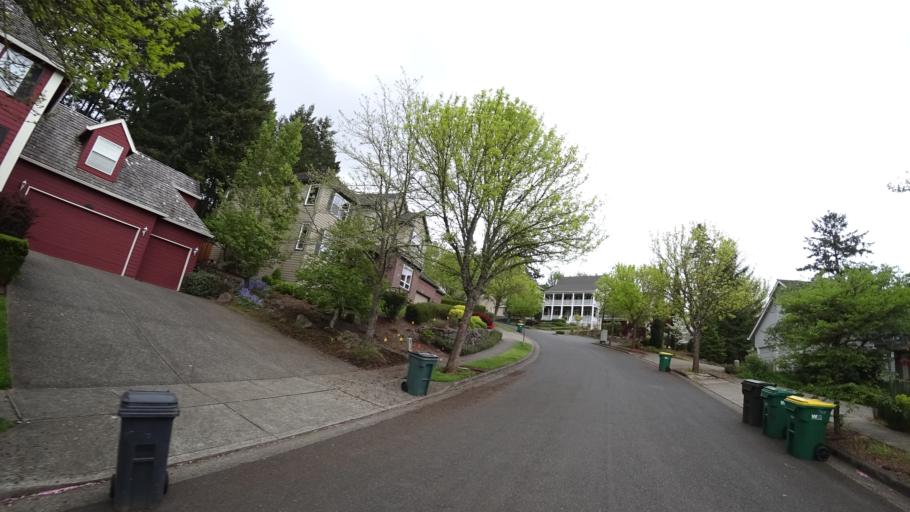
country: US
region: Oregon
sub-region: Washington County
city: Beaverton
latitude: 45.4593
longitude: -122.8311
